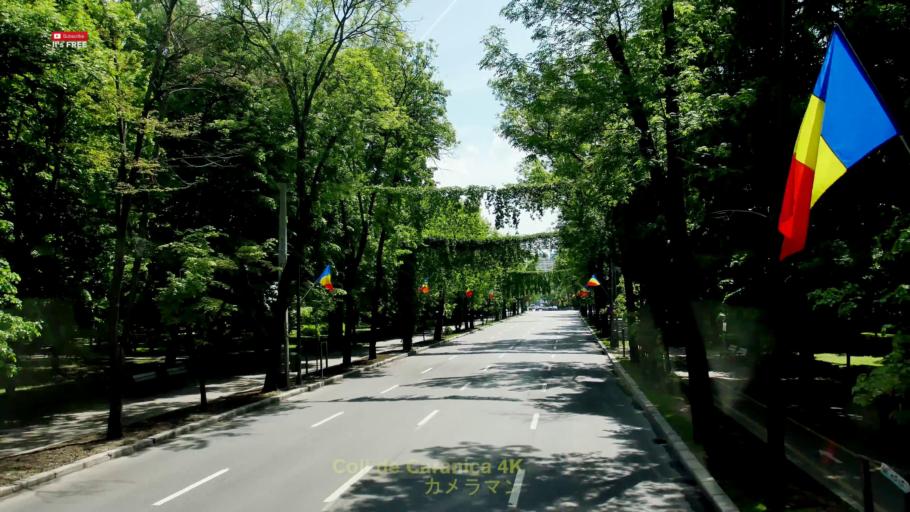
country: RO
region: Bucuresti
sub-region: Municipiul Bucuresti
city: Bucuresti
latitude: 44.4582
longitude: 26.0826
